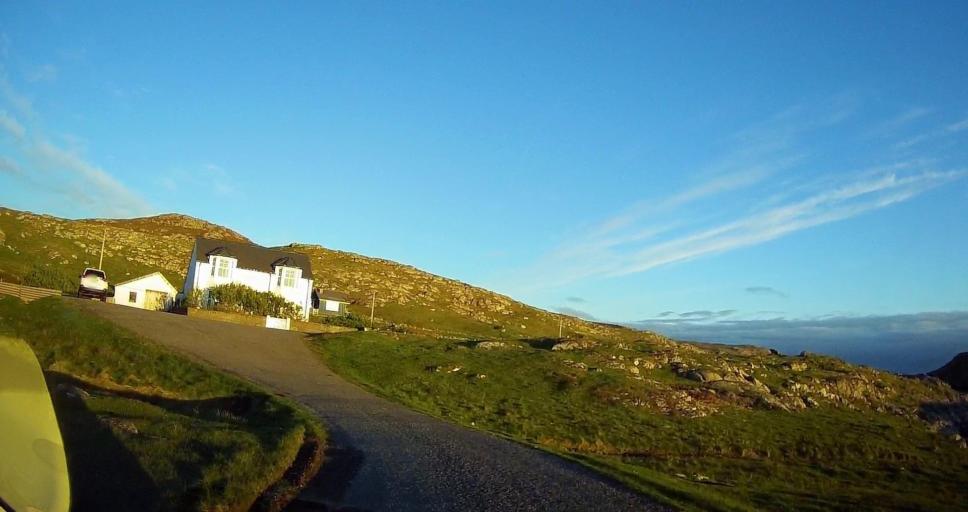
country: GB
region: Scotland
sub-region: Shetland Islands
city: Lerwick
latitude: 60.4413
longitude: -1.4480
